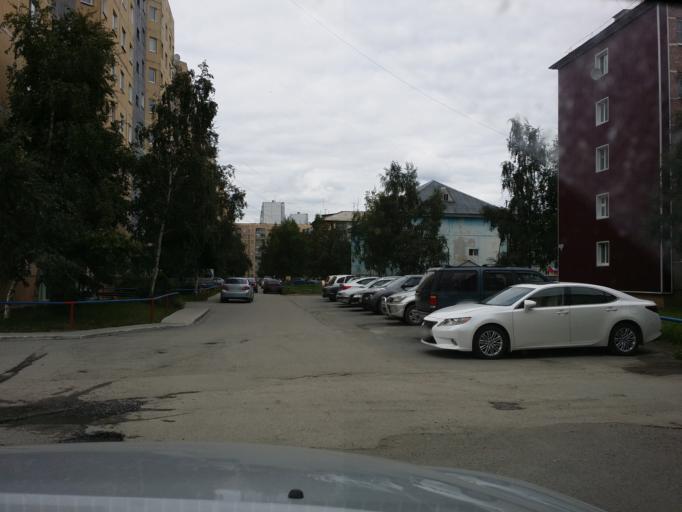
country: RU
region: Khanty-Mansiyskiy Avtonomnyy Okrug
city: Nizhnevartovsk
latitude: 60.9291
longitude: 76.5858
